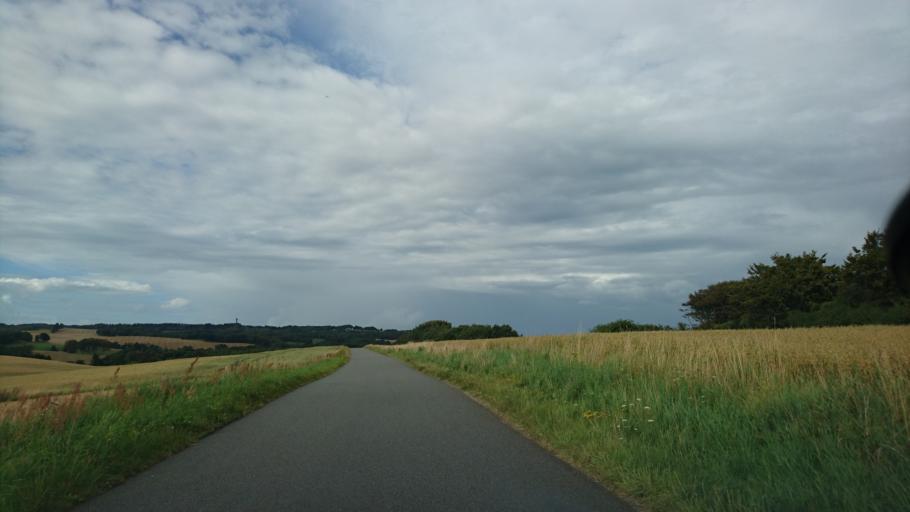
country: DK
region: North Denmark
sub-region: Frederikshavn Kommune
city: Saeby
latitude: 57.3927
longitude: 10.4782
